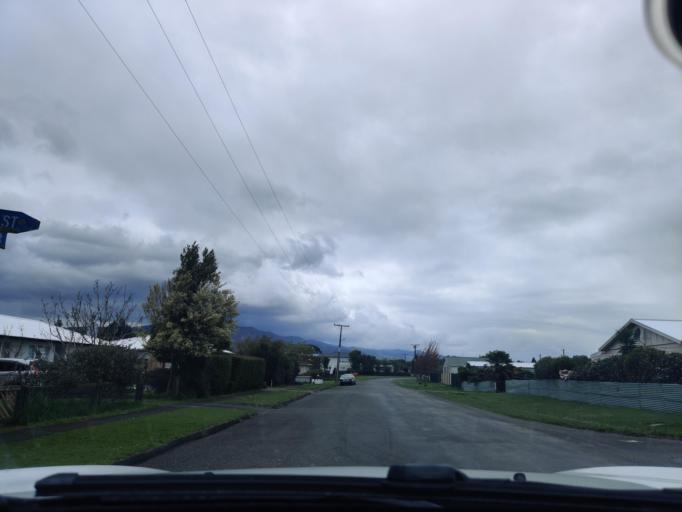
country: NZ
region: Manawatu-Wanganui
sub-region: Palmerston North City
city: Palmerston North
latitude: -40.3356
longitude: 175.8643
